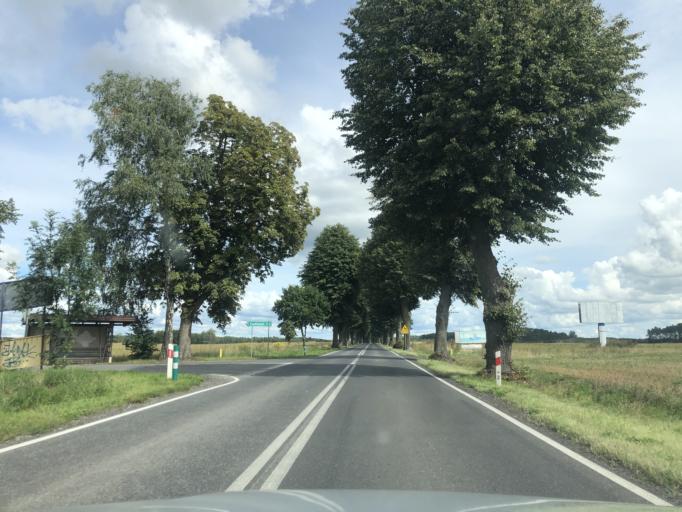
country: PL
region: Greater Poland Voivodeship
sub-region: Powiat czarnkowsko-trzcianecki
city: Trzcianka
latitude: 53.0538
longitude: 16.5000
